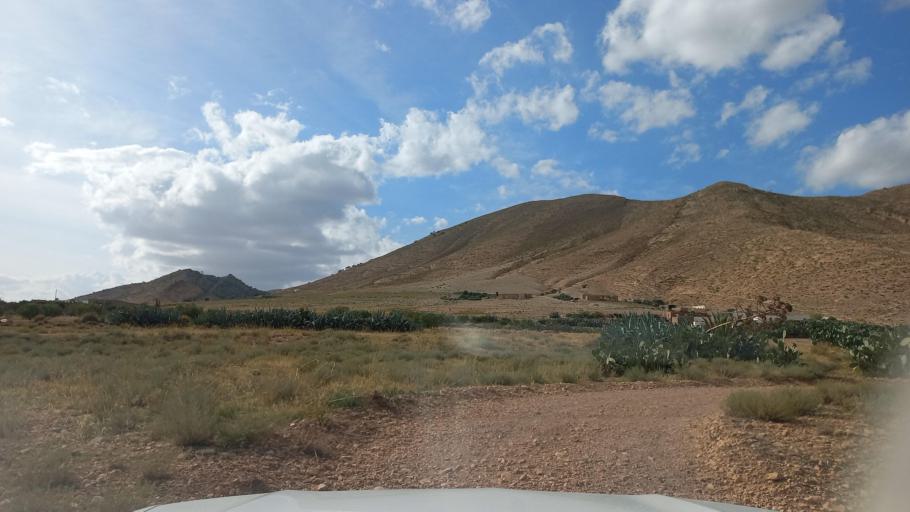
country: TN
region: Al Qasrayn
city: Sbiba
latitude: 35.4554
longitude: 9.0700
